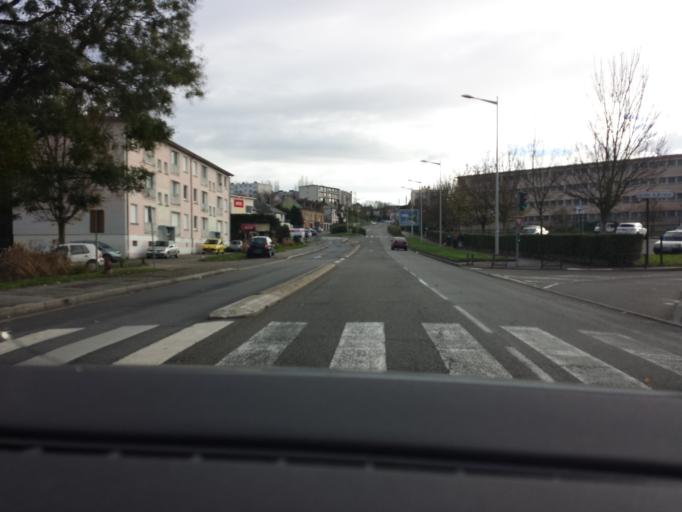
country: FR
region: Haute-Normandie
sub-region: Departement de l'Eure
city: Evreux
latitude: 49.0182
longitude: 1.1564
